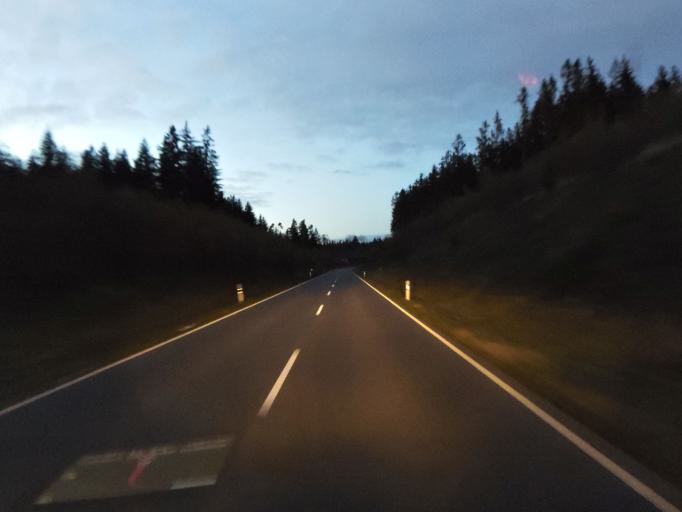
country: DE
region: Bavaria
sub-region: Upper Bavaria
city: Brunnthal
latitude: 48.0176
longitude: 11.6960
